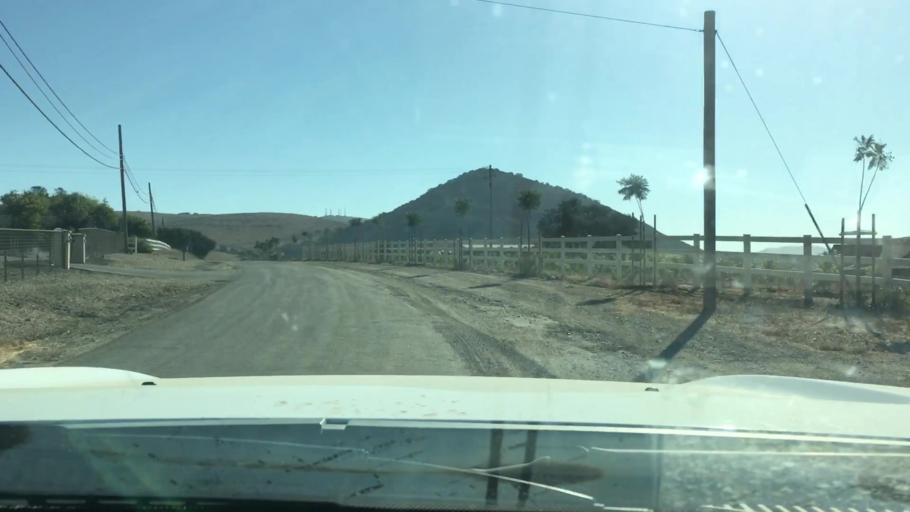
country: US
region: California
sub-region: San Luis Obispo County
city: Arroyo Grande
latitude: 35.1043
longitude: -120.5571
